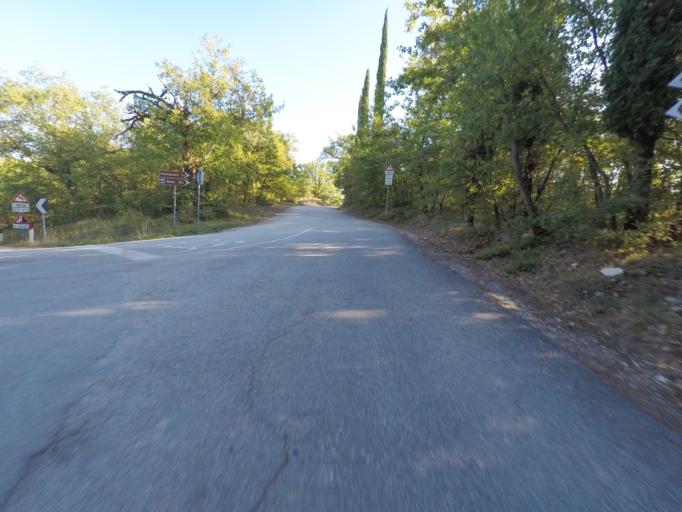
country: IT
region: Tuscany
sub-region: Provincia di Siena
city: Gaiole in Chianti
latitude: 43.4422
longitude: 11.3947
